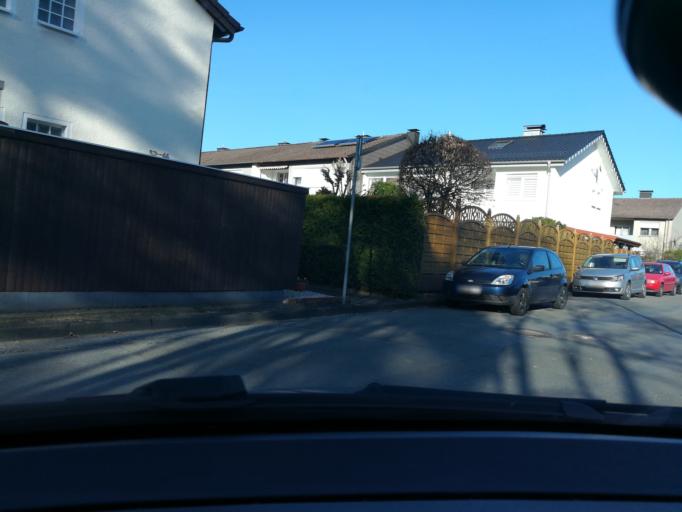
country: DE
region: North Rhine-Westphalia
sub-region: Regierungsbezirk Detmold
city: Oerlinghausen
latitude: 51.9562
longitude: 8.5855
